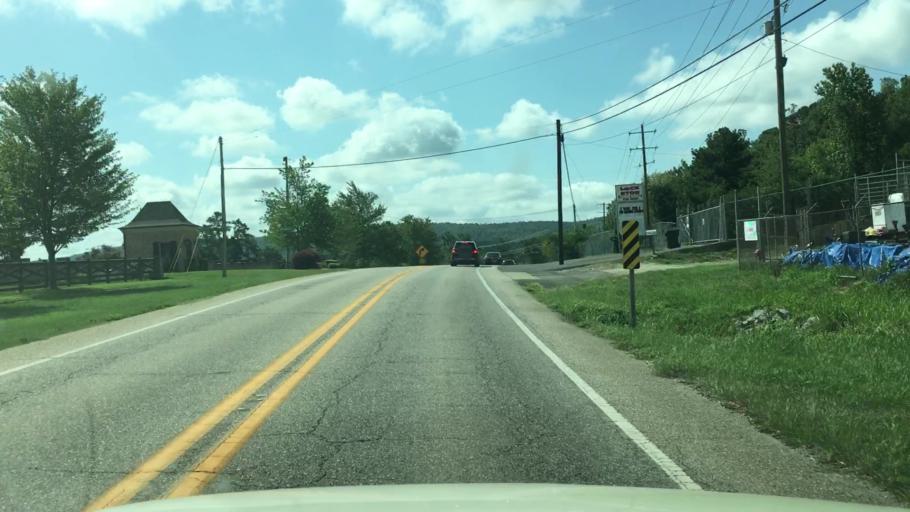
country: US
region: Arkansas
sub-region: Garland County
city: Lake Hamilton
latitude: 34.4078
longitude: -93.0916
